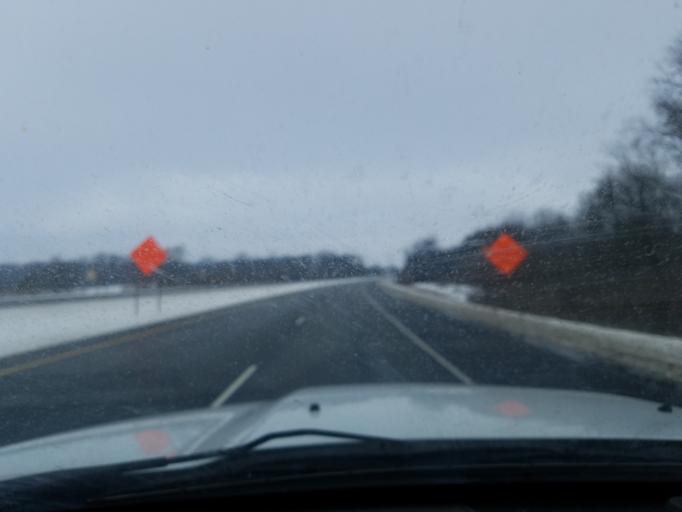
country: US
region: Indiana
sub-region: Marshall County
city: Argos
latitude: 41.2756
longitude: -86.2711
